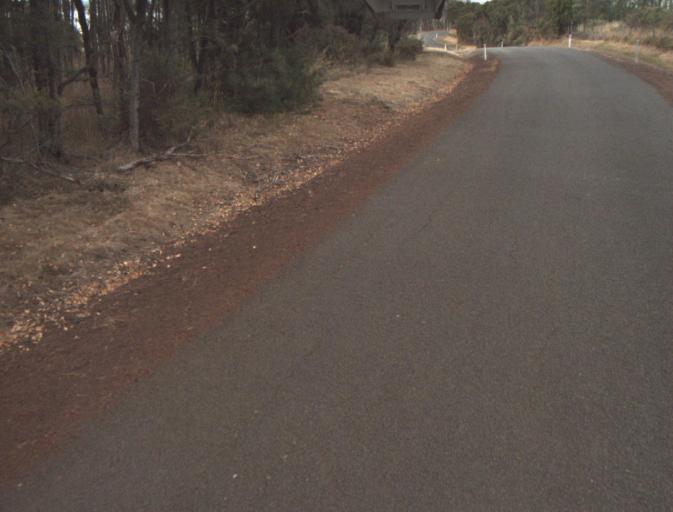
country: AU
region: Tasmania
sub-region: Launceston
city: Mayfield
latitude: -41.2919
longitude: 146.9908
